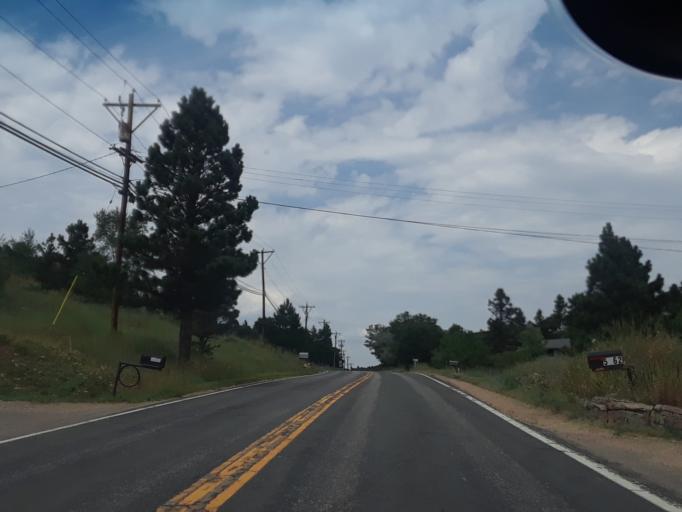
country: US
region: Colorado
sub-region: Boulder County
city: Boulder
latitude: 40.0756
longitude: -105.3013
